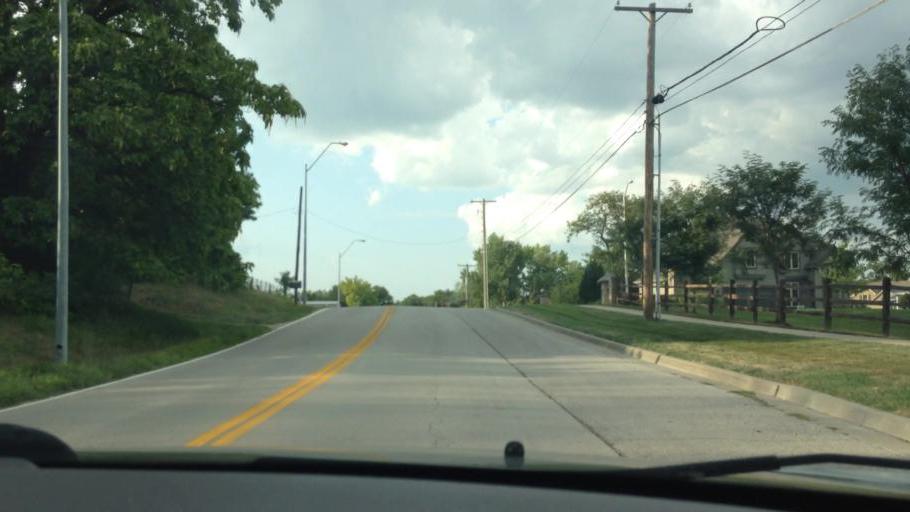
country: US
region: Missouri
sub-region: Platte County
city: Parkville
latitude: 39.2219
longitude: -94.6404
